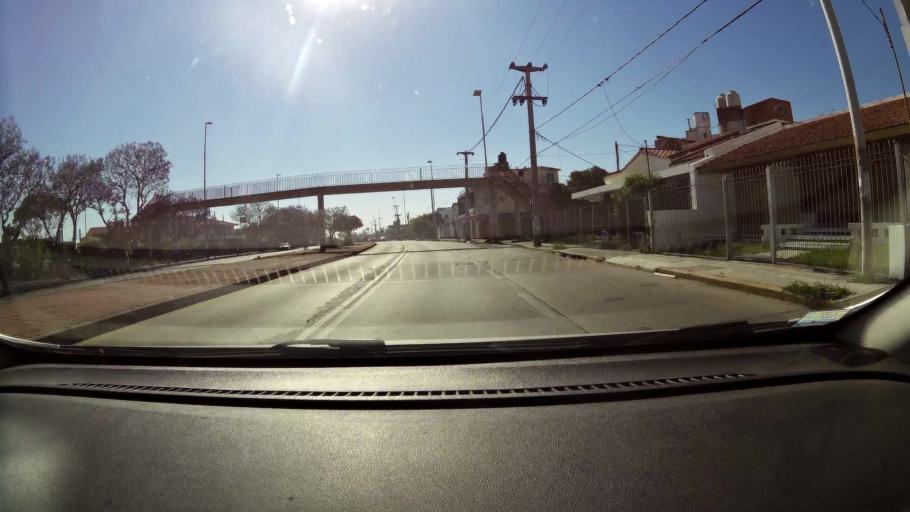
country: AR
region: Cordoba
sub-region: Departamento de Capital
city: Cordoba
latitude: -31.4331
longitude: -64.1611
